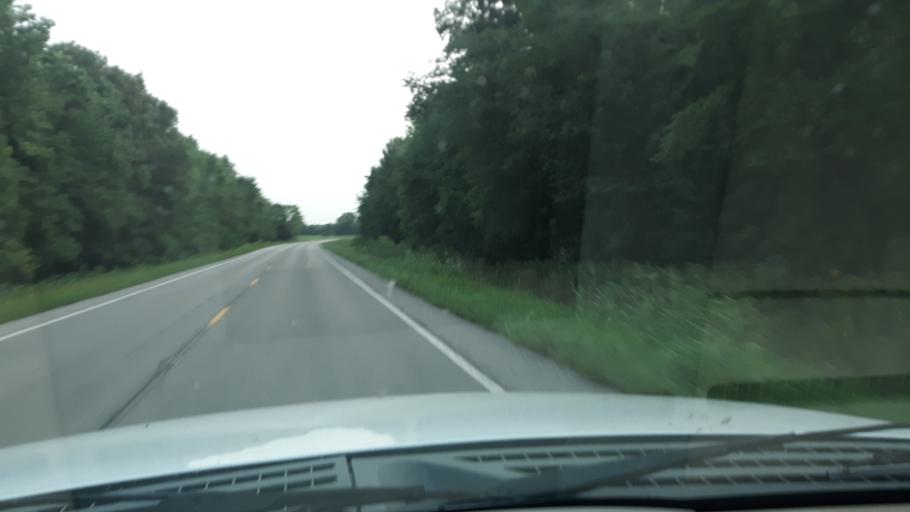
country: US
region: Illinois
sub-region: White County
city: Norris City
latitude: 37.9736
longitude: -88.3200
